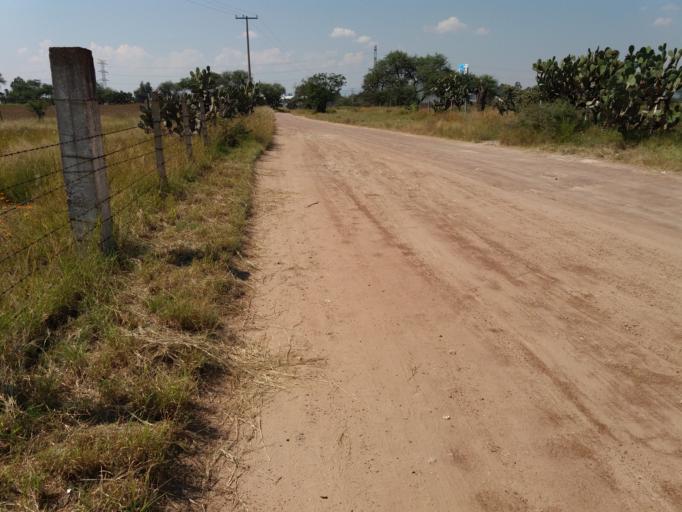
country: MX
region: Aguascalientes
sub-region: Aguascalientes
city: Penuelas (El Cienegal)
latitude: 21.7603
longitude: -102.2739
